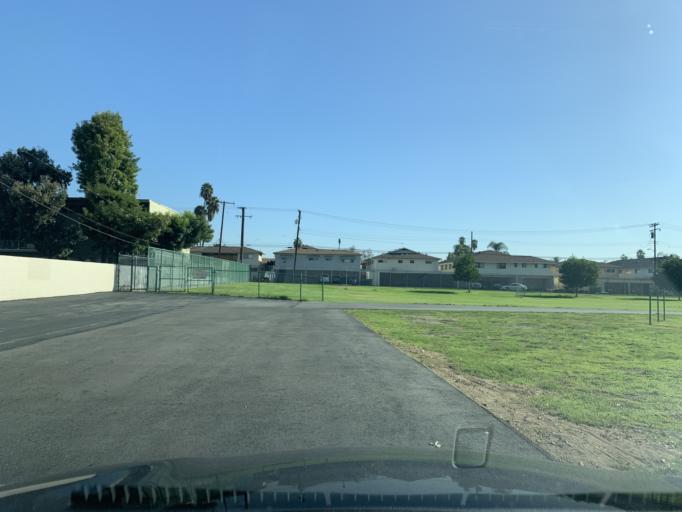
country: US
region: California
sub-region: Los Angeles County
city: Covina
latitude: 34.0891
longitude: -117.8802
